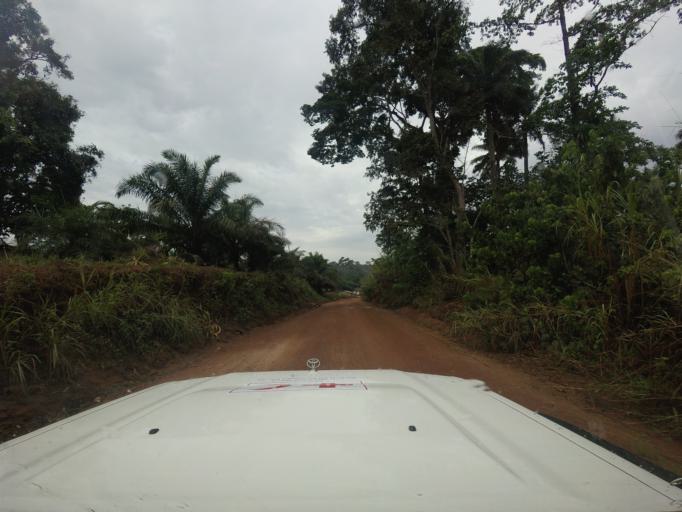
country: SL
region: Eastern Province
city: Buedu
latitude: 8.3359
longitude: -10.1683
